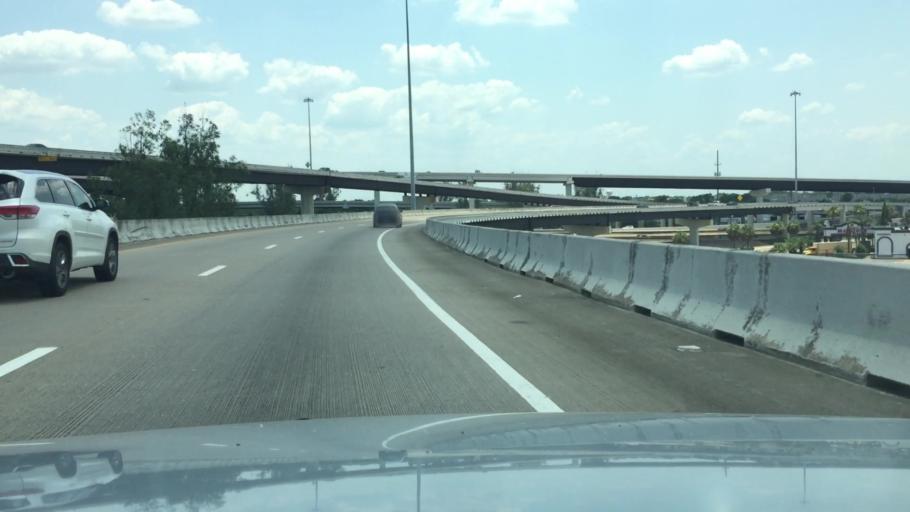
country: US
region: Texas
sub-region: Fort Bend County
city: Meadows Place
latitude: 29.6625
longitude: -95.5592
